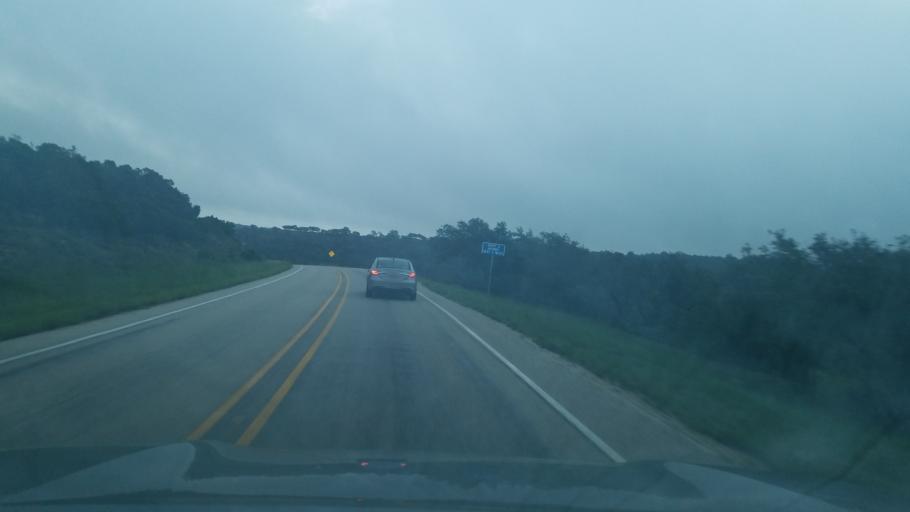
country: US
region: Texas
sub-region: Blanco County
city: Blanco
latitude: 30.1410
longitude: -98.2667
